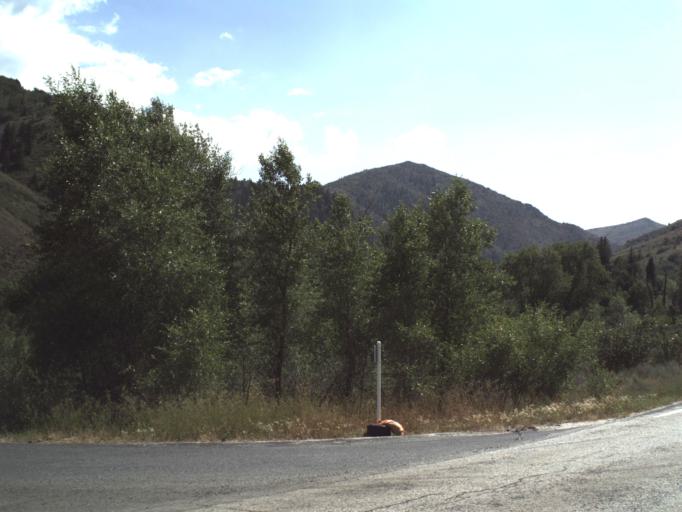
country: US
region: Utah
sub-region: Weber County
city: Wolf Creek
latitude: 41.2843
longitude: -111.6509
